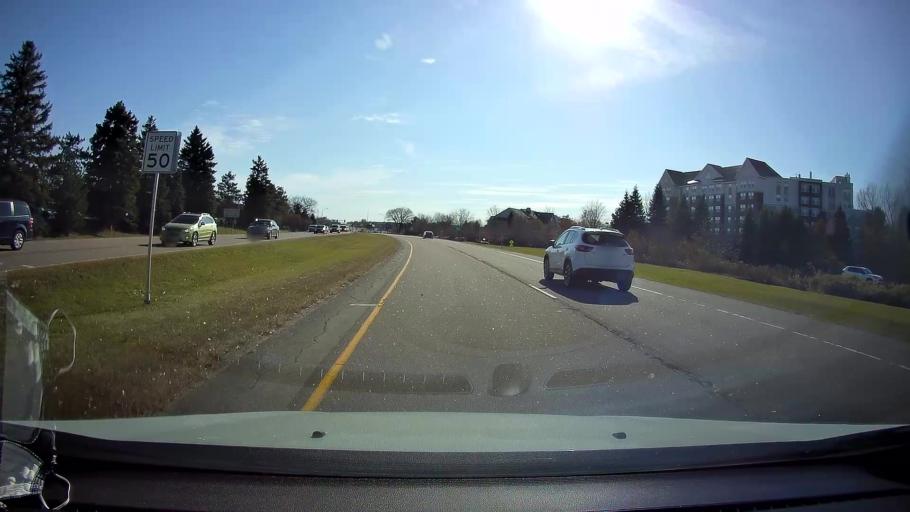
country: US
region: Minnesota
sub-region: Ramsey County
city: Arden Hills
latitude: 45.0306
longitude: -93.1669
